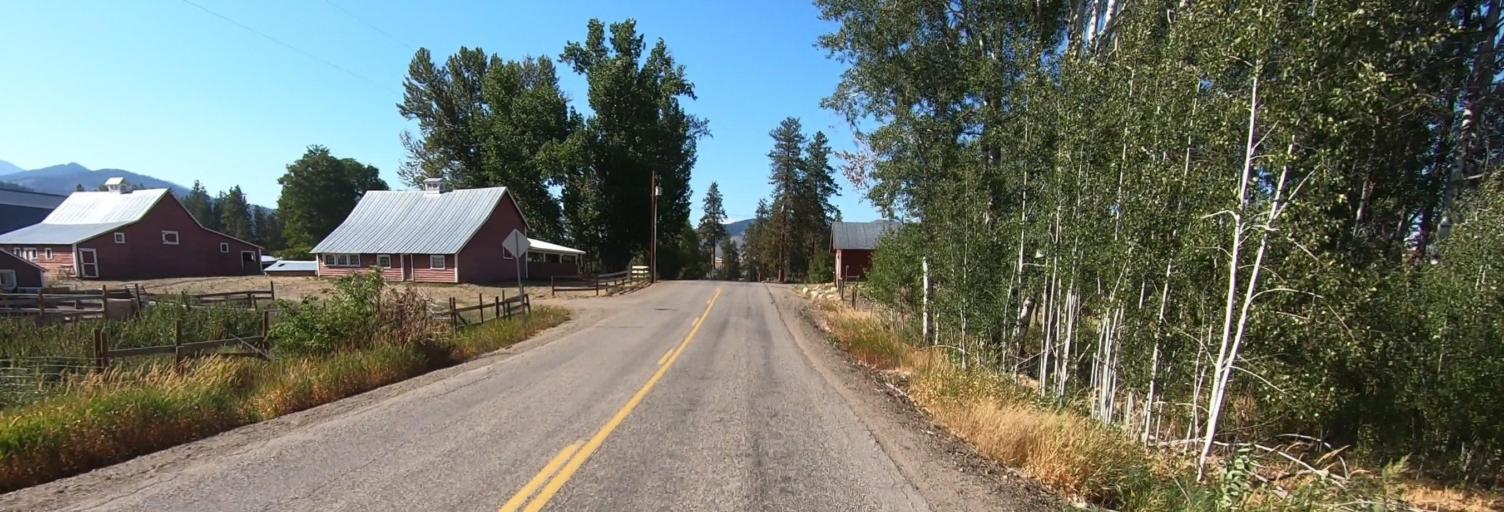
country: US
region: Washington
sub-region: Okanogan County
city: Brewster
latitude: 48.4713
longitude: -120.2046
